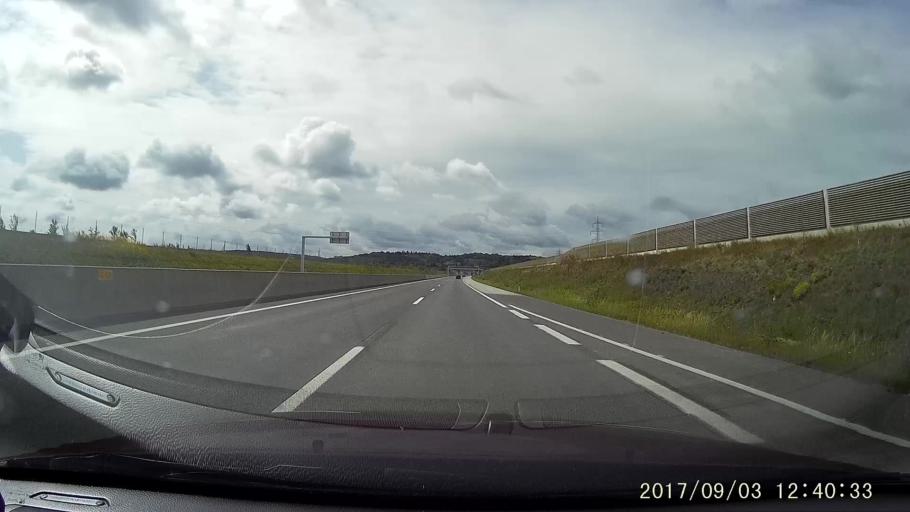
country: AT
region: Lower Austria
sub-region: Politischer Bezirk Korneuburg
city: Enzersfeld
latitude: 48.3446
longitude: 16.4348
